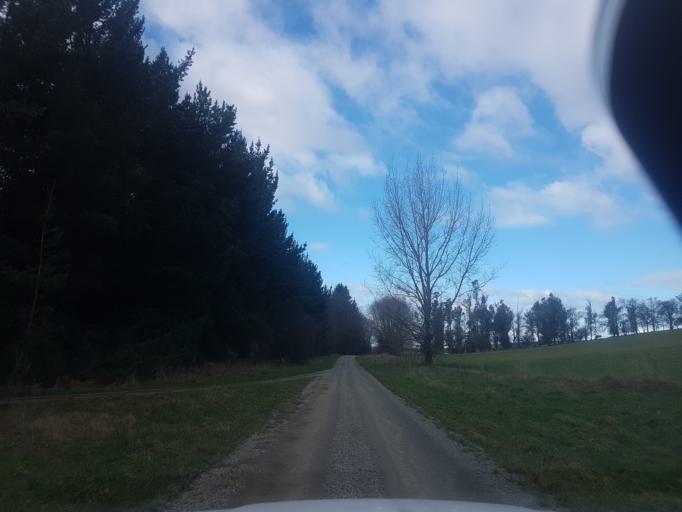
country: NZ
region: Canterbury
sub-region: Timaru District
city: Pleasant Point
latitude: -44.1872
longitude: 171.1572
